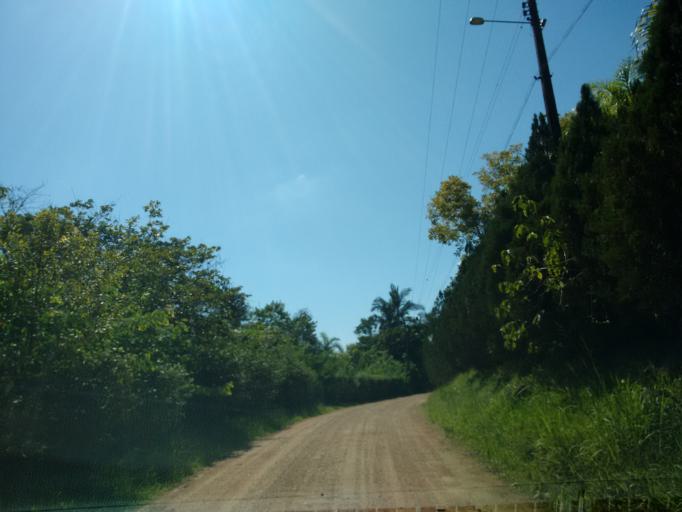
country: BR
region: Santa Catarina
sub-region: Indaial
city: Indaial
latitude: -26.9147
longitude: -49.1911
